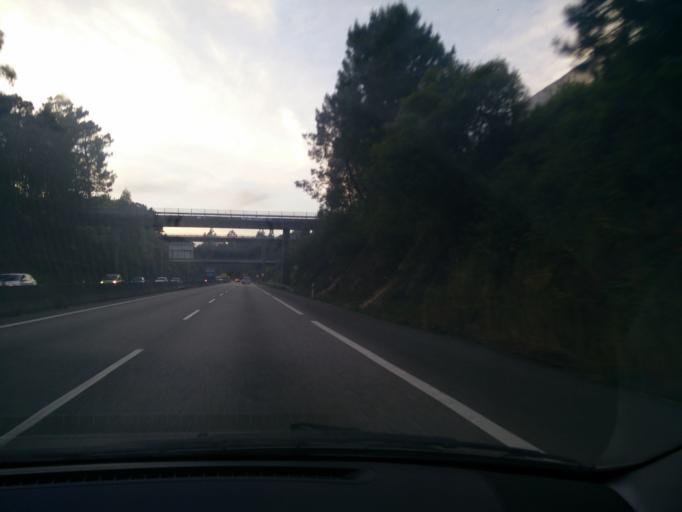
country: ES
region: Galicia
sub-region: Provincia de Pontevedra
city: Porrino
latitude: 42.1779
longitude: -8.6256
